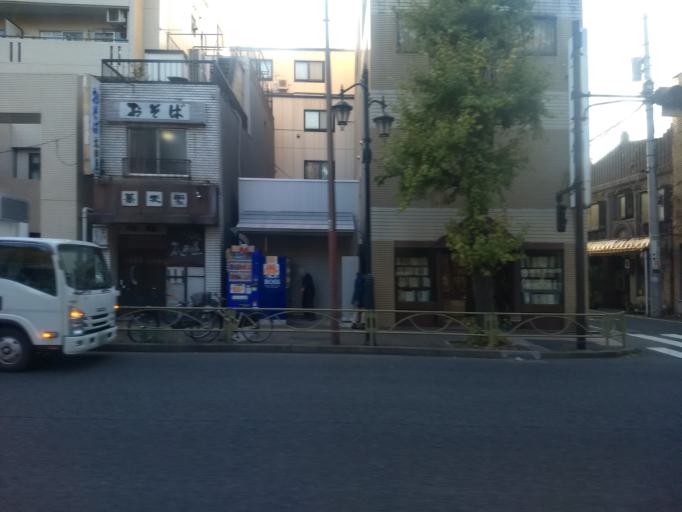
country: JP
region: Tokyo
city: Tokyo
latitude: 35.7129
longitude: 139.7592
